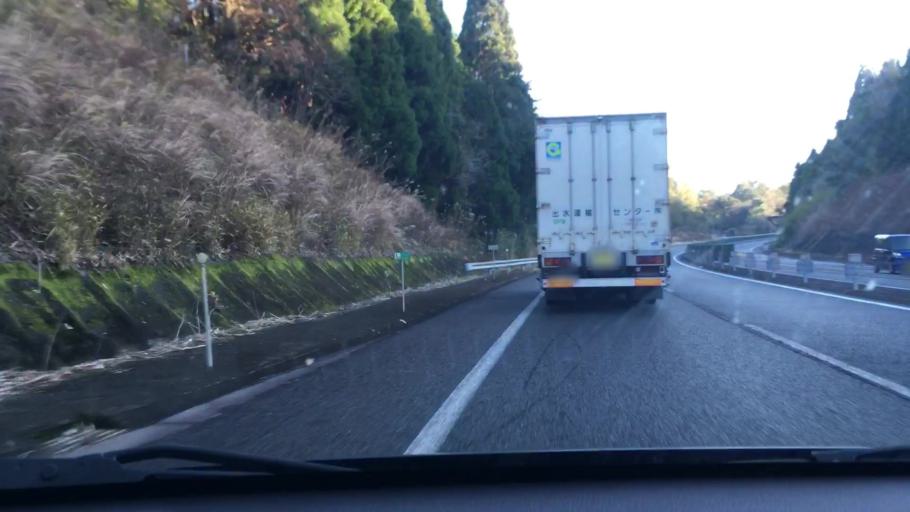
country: JP
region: Kagoshima
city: Kajiki
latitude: 31.8318
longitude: 130.6927
